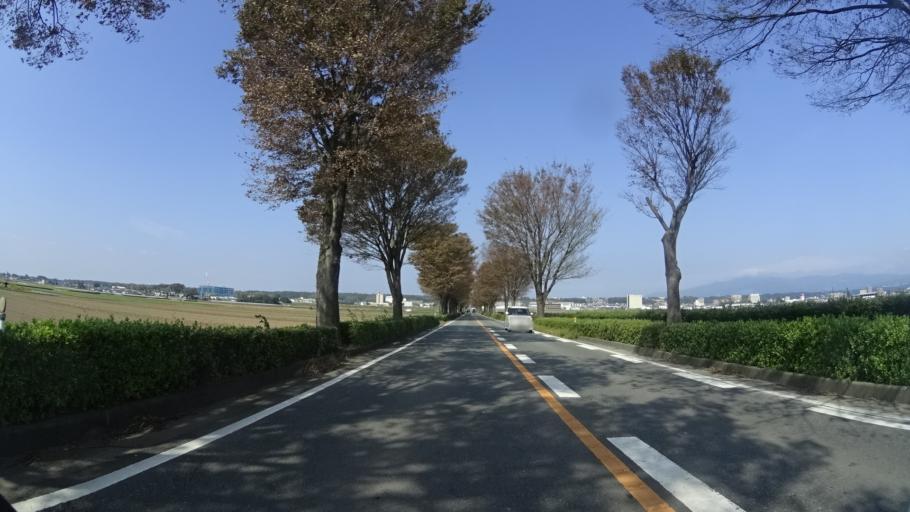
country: JP
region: Kumamoto
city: Ozu
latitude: 32.8660
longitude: 130.8553
